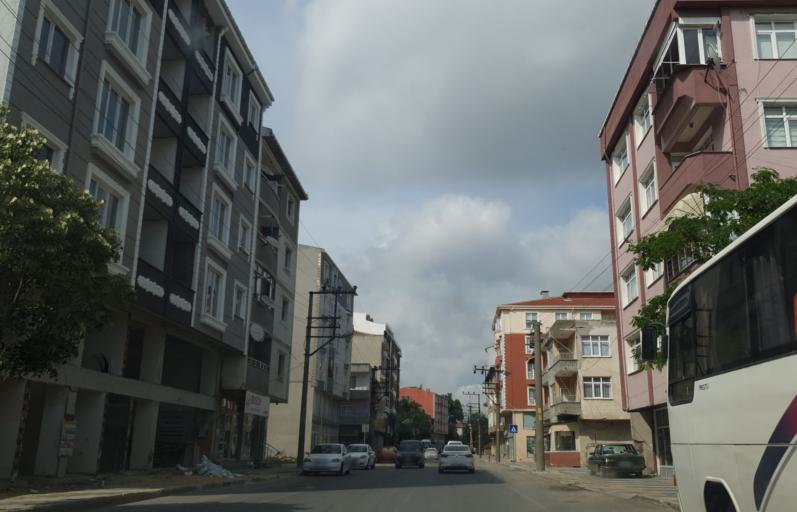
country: TR
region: Tekirdag
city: Saray
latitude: 41.4451
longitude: 27.9265
